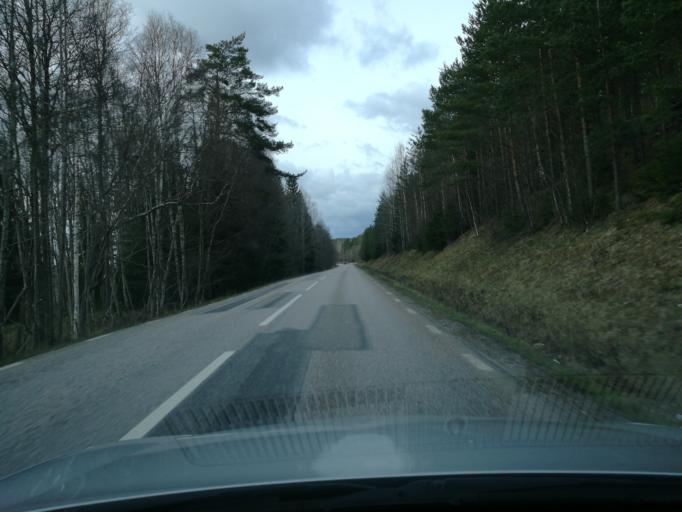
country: SE
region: Soedermanland
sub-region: Gnesta Kommun
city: Gnesta
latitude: 58.9128
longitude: 17.3325
